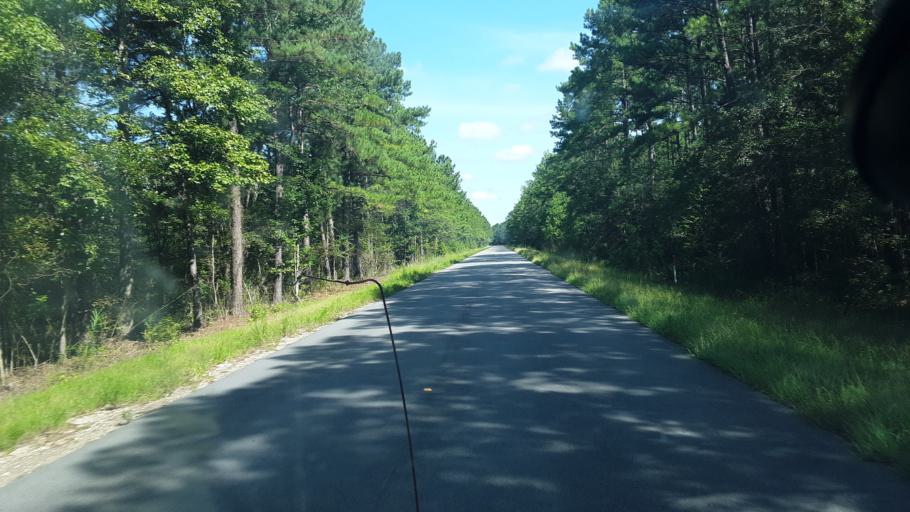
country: US
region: South Carolina
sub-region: Hampton County
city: Varnville
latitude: 32.7226
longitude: -81.0301
